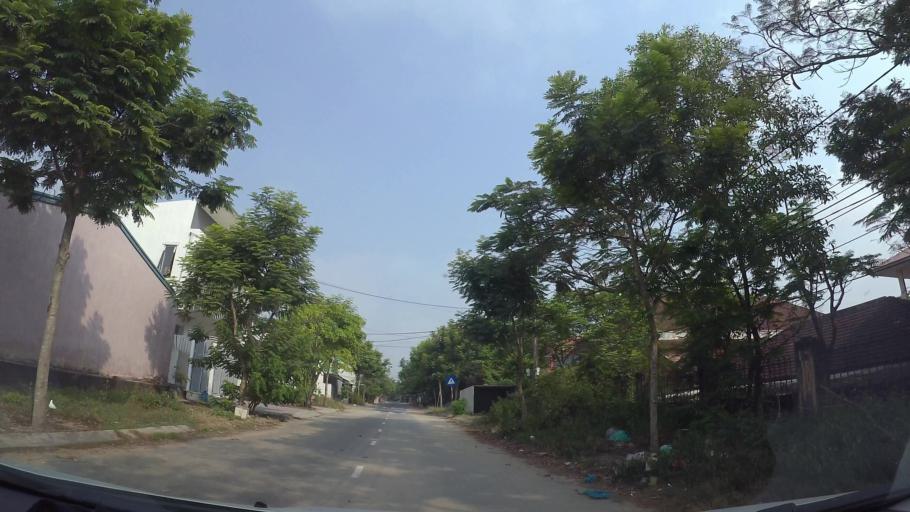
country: VN
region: Da Nang
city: Ngu Hanh Son
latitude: 16.0282
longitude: 108.2462
